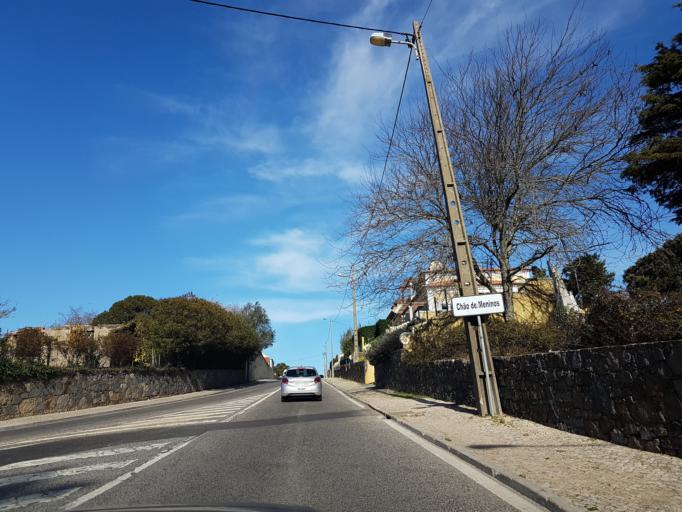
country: PT
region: Lisbon
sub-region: Sintra
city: Sintra
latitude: 38.7897
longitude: -9.3737
